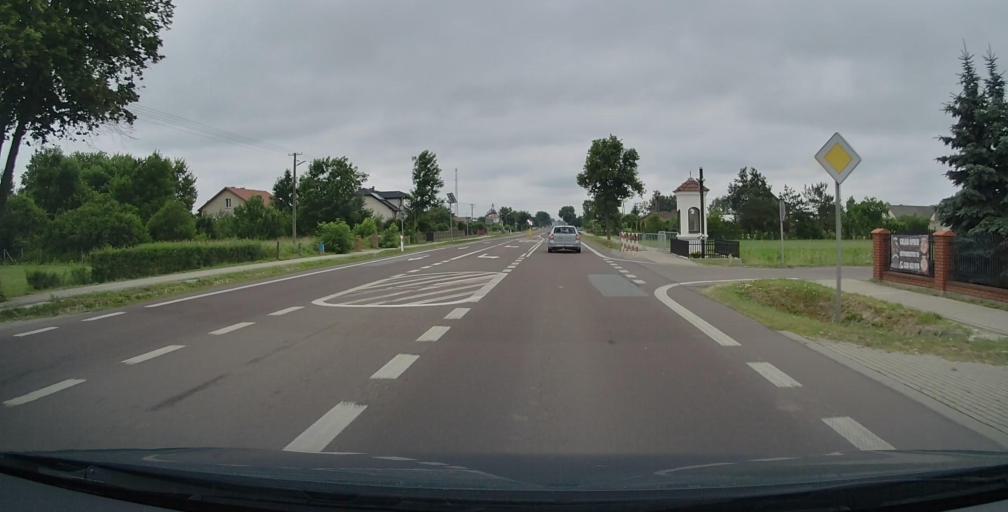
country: PL
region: Lublin Voivodeship
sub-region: Powiat bialski
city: Rzeczyca
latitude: 52.0301
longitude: 22.7070
